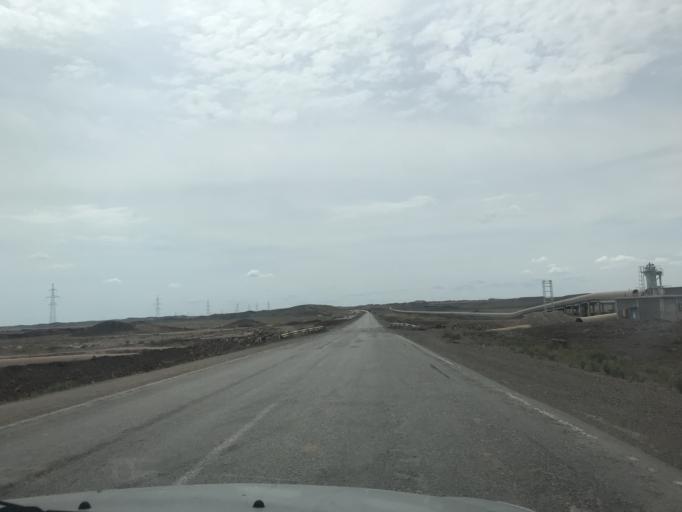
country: KZ
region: Zhambyl
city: Mynaral
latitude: 45.3833
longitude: 73.6509
